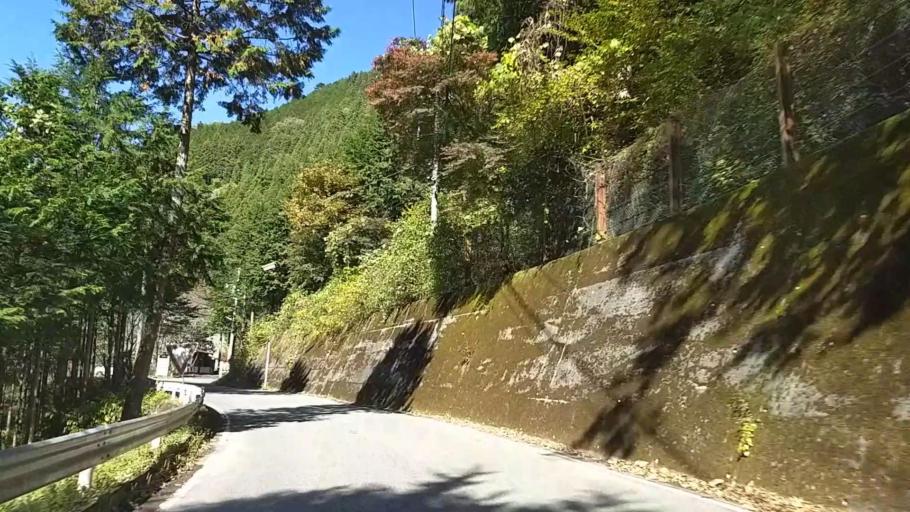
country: JP
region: Yamanashi
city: Uenohara
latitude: 35.6825
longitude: 139.0523
